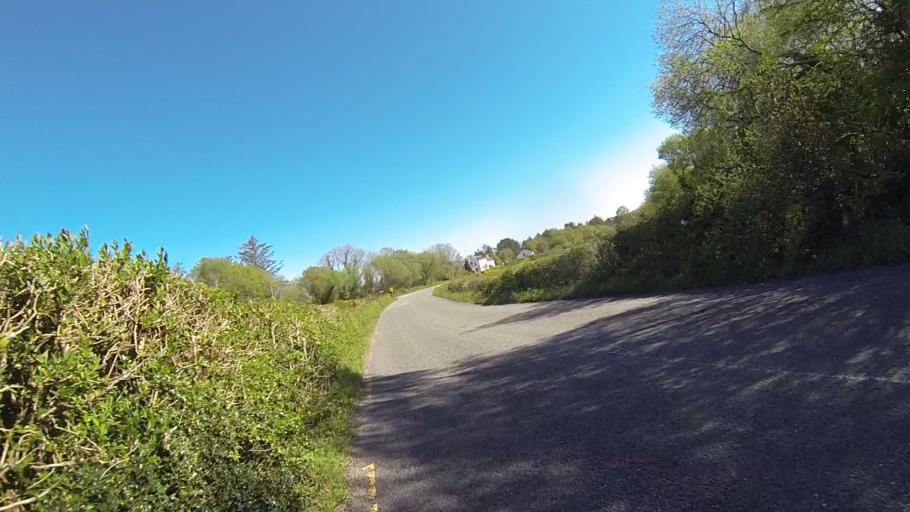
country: IE
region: Munster
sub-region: Ciarrai
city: Kenmare
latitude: 51.8171
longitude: -9.7417
